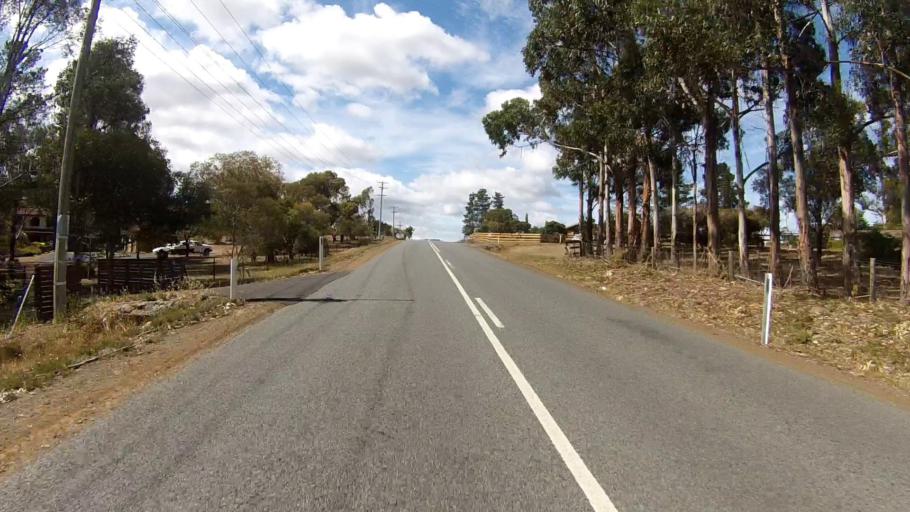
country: AU
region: Tasmania
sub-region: Brighton
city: Bridgewater
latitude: -42.7138
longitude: 147.2732
